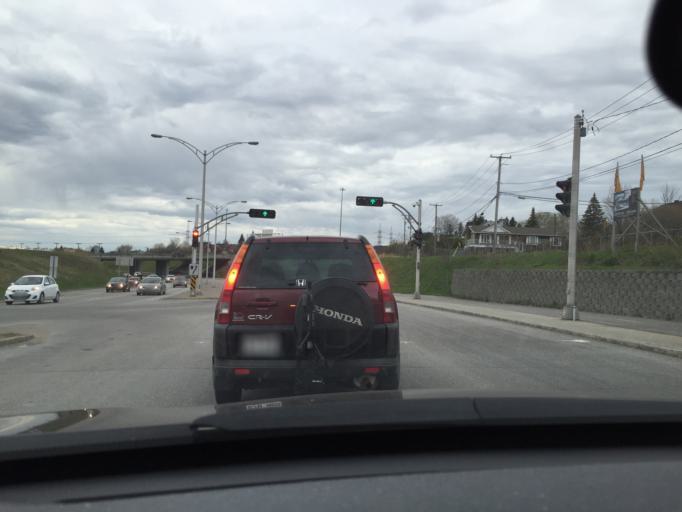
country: CA
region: Quebec
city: Quebec
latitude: 46.8470
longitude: -71.2712
